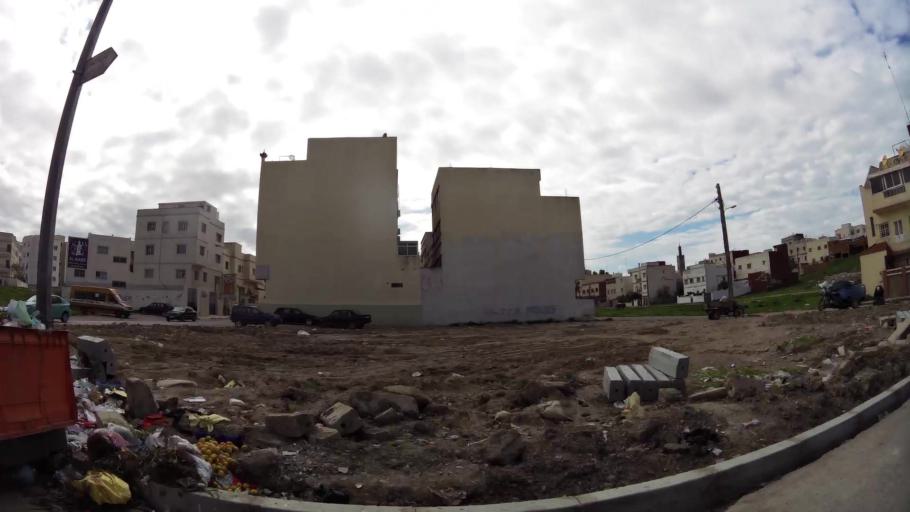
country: MA
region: Tanger-Tetouan
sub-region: Tanger-Assilah
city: Tangier
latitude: 35.7625
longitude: -5.8074
